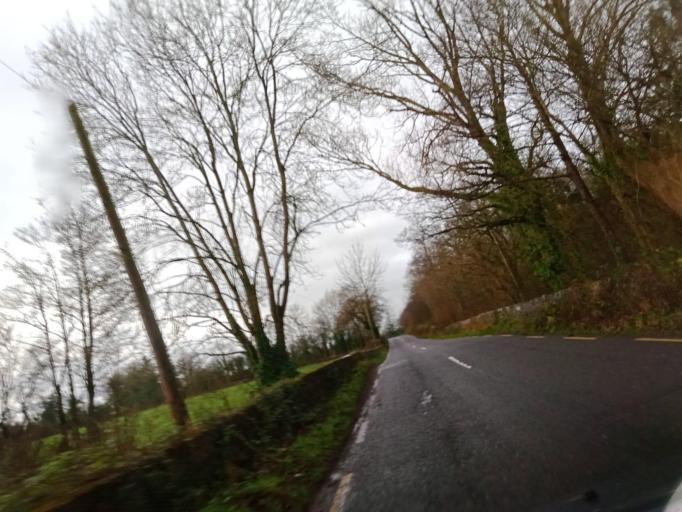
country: IE
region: Leinster
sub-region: Kilkenny
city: Callan
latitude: 52.5781
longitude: -7.3559
